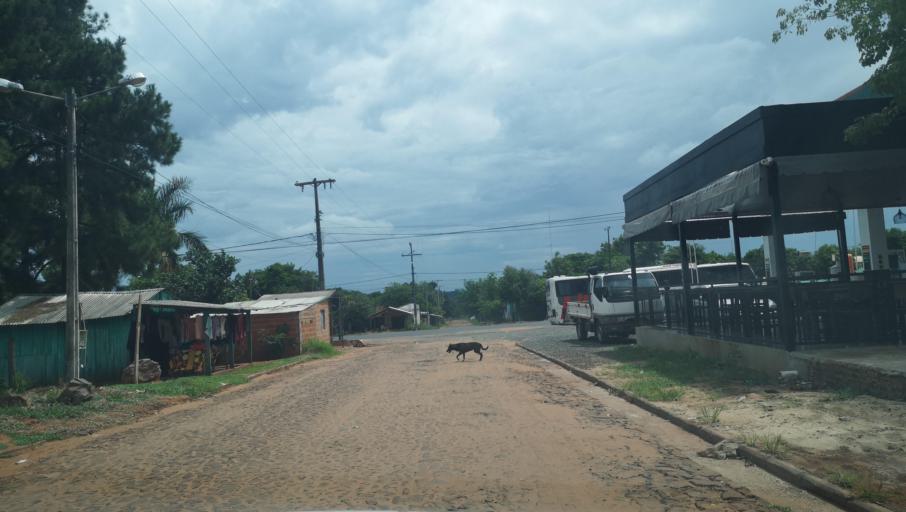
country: PY
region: San Pedro
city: Capiibary
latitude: -24.7239
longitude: -56.0162
